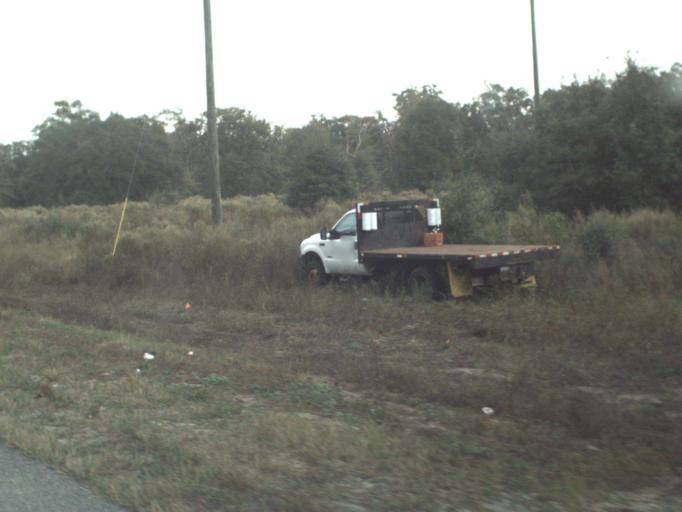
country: US
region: Florida
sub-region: Wakulla County
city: Crawfordville
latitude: 30.1250
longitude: -84.3668
